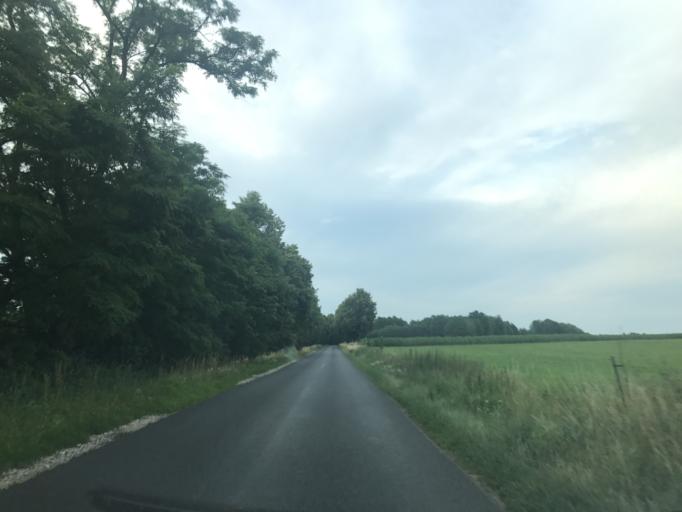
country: PL
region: Kujawsko-Pomorskie
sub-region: Powiat lipnowski
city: Lipno
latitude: 52.8149
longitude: 19.1838
